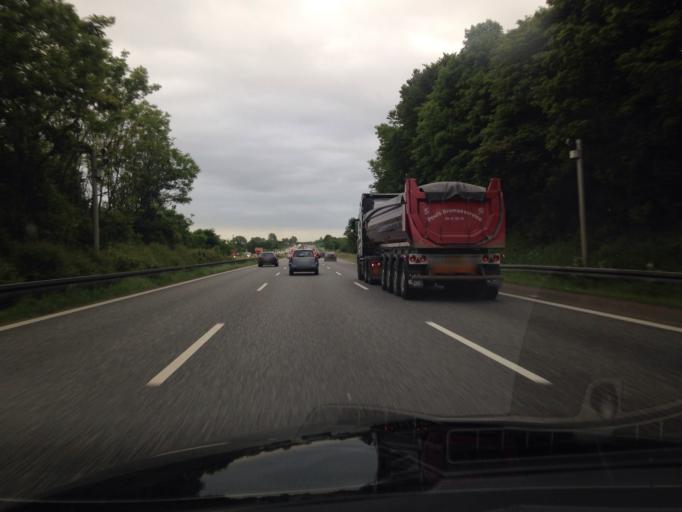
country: DK
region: South Denmark
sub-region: Fredericia Kommune
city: Snoghoj
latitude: 55.5392
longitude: 9.6725
